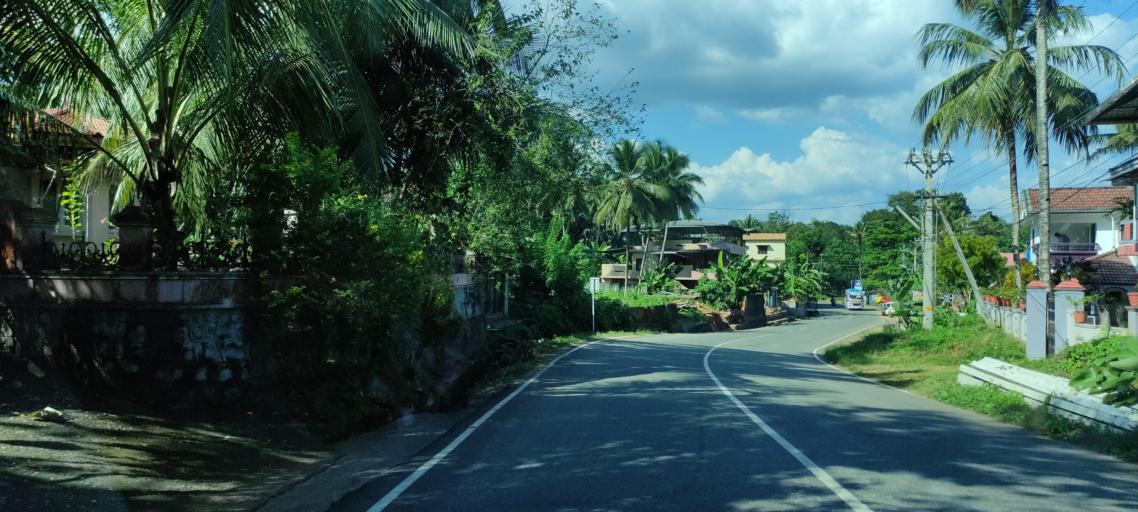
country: IN
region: Kerala
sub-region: Pattanamtitta
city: Pathanamthitta
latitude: 9.2290
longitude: 76.7541
